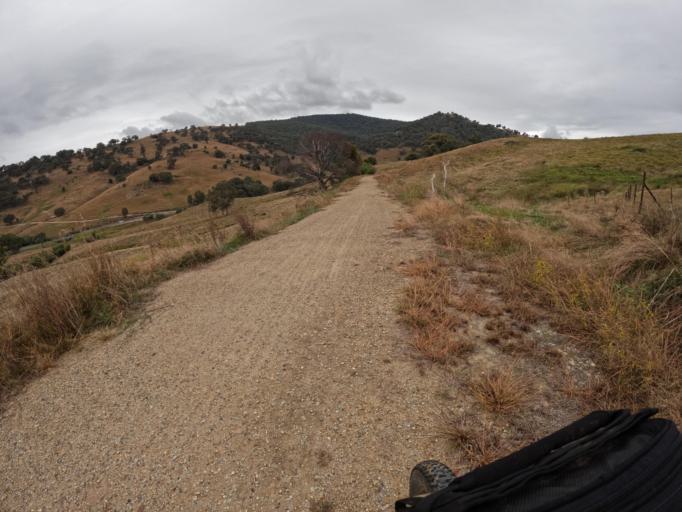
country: AU
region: New South Wales
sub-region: Albury Municipality
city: East Albury
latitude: -36.1858
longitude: 147.3662
